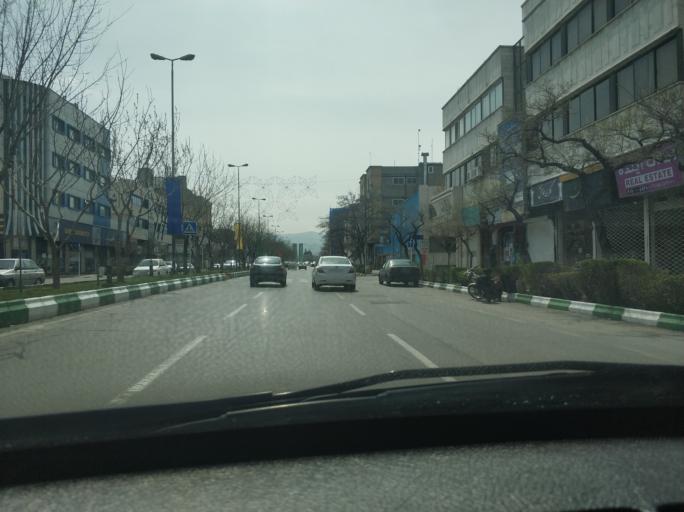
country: IR
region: Razavi Khorasan
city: Mashhad
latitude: 36.3031
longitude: 59.5647
